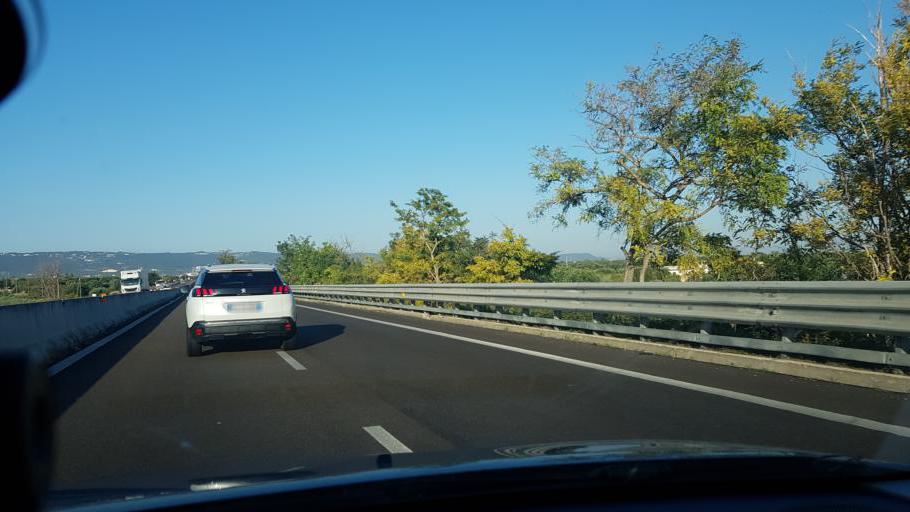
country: IT
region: Apulia
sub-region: Provincia di Brindisi
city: Pezze di Greco
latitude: 40.8337
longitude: 17.4149
